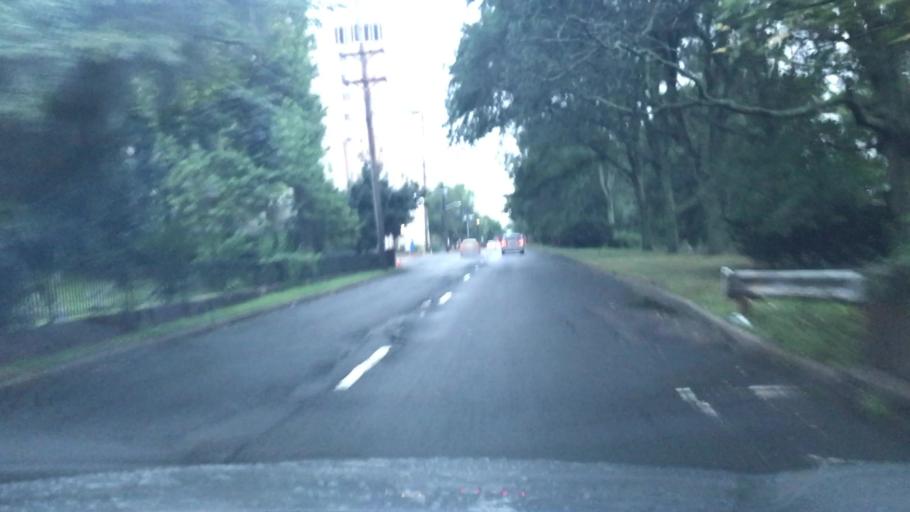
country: US
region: New Jersey
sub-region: Bergen County
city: Englewood
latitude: 40.9066
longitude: -73.9690
